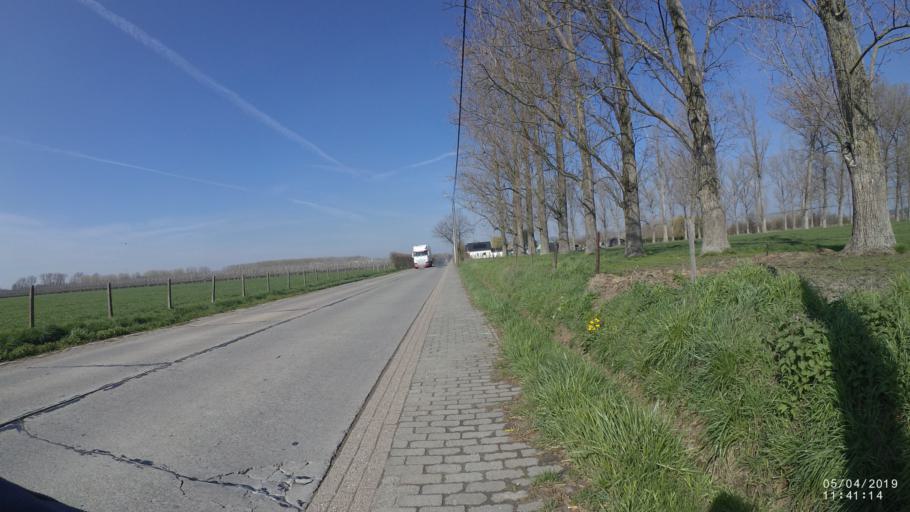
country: BE
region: Flanders
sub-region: Provincie Vlaams-Brabant
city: Geetbets
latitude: 50.8964
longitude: 5.1523
